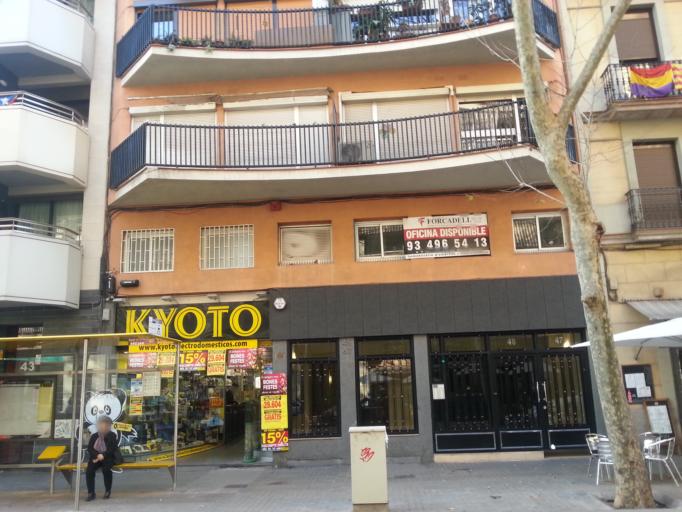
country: ES
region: Catalonia
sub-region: Provincia de Barcelona
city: Ciutat Vella
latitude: 41.3919
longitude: 2.1886
